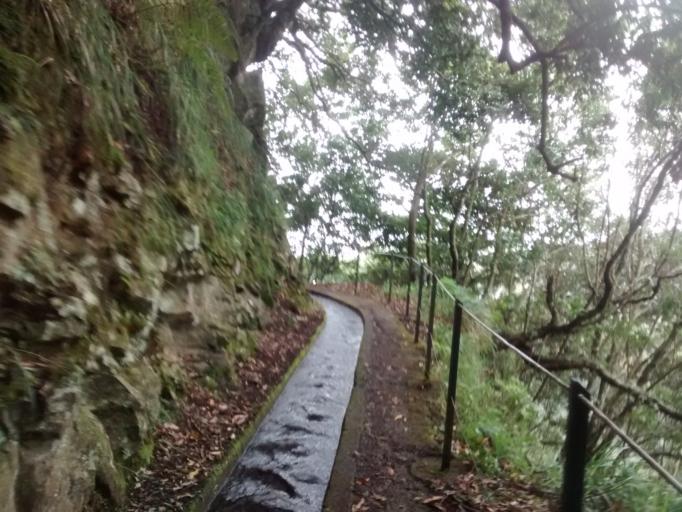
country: PT
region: Madeira
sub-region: Santana
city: Santana
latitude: 32.8096
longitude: -16.9326
